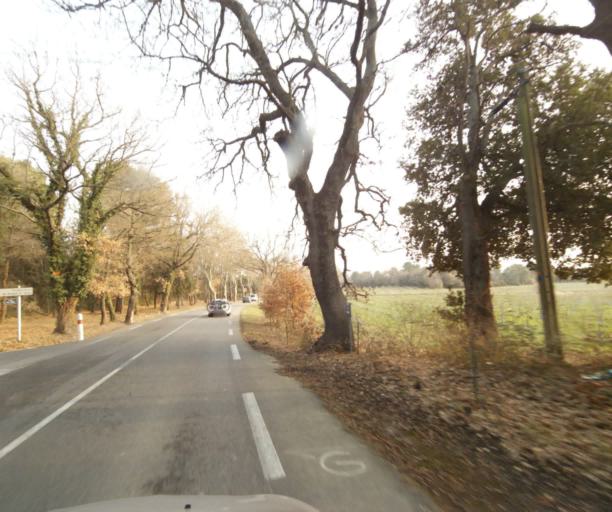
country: FR
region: Provence-Alpes-Cote d'Azur
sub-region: Departement des Bouches-du-Rhone
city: Eguilles
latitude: 43.6112
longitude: 5.3648
